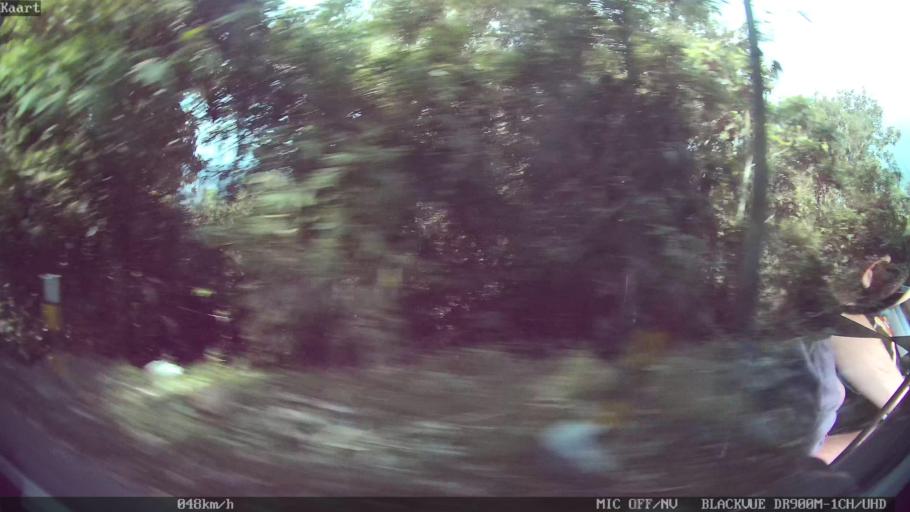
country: ID
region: Bali
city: Subuk
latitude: -8.3009
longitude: 114.9783
